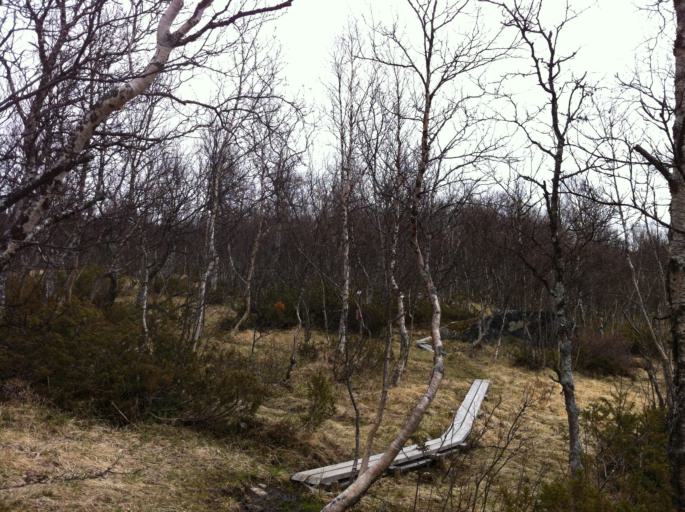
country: NO
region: Sor-Trondelag
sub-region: Tydal
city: Aas
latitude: 62.5560
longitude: 12.3124
